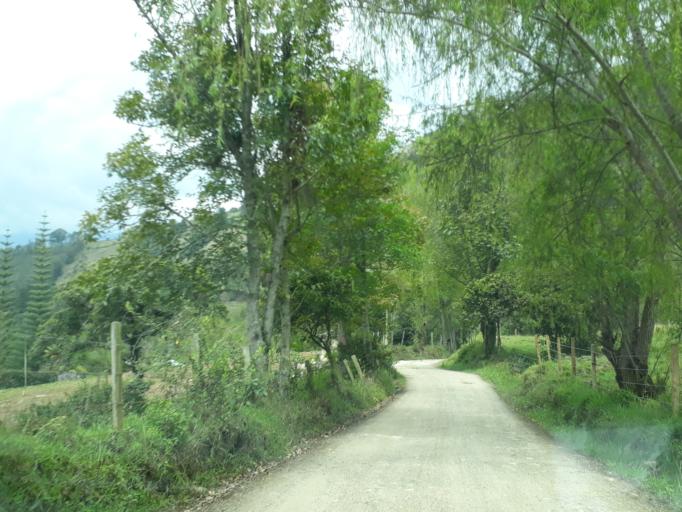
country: CO
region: Cundinamarca
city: Macheta
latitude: 5.0911
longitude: -73.5711
